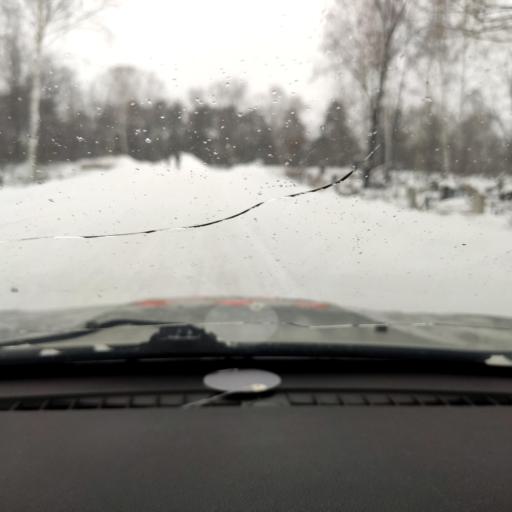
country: RU
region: Samara
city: Tol'yatti
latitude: 53.5029
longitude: 49.4516
